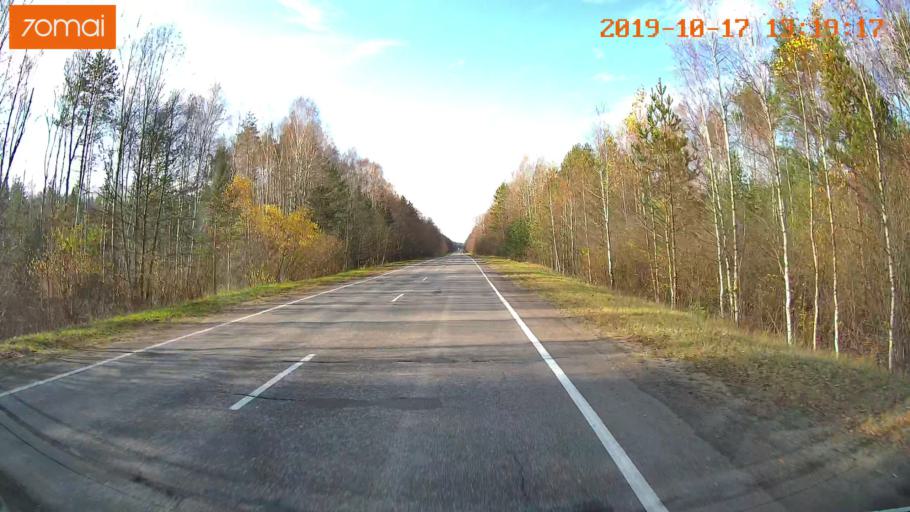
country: RU
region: Rjazan
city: Gus'-Zheleznyy
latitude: 55.0684
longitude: 41.0779
